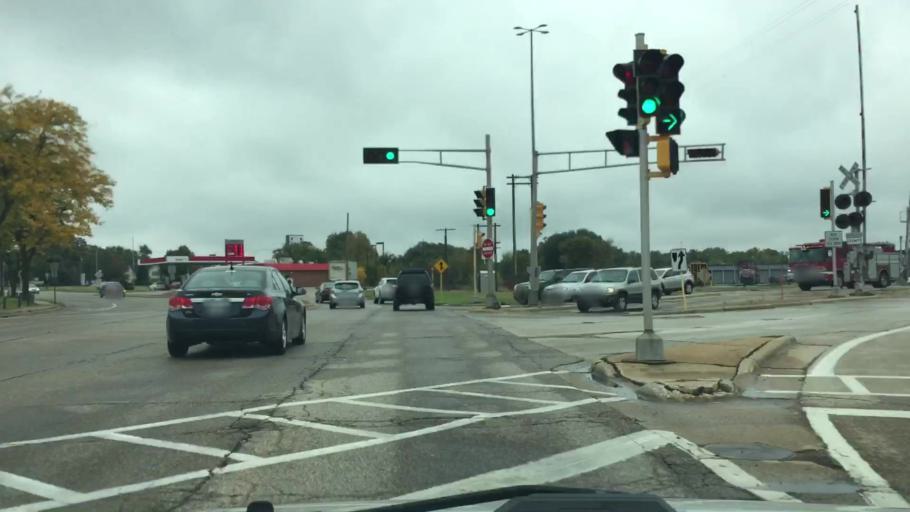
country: US
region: Wisconsin
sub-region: Rock County
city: Janesville
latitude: 42.6796
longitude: -89.0317
